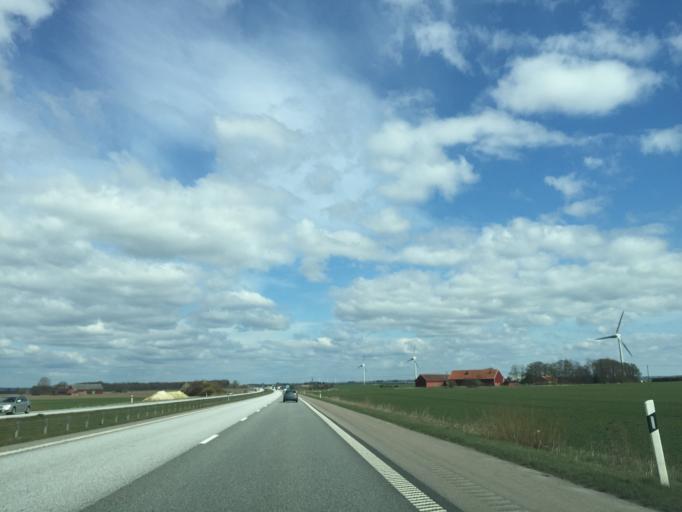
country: SE
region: Skane
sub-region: Eslovs Kommun
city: Eslov
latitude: 55.7527
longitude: 13.2762
